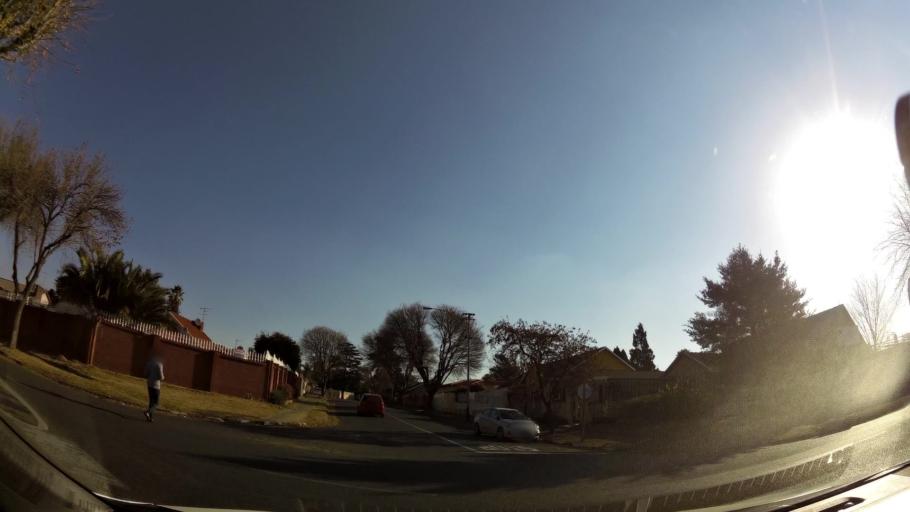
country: ZA
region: Gauteng
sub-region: City of Johannesburg Metropolitan Municipality
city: Johannesburg
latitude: -26.2414
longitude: 28.0262
